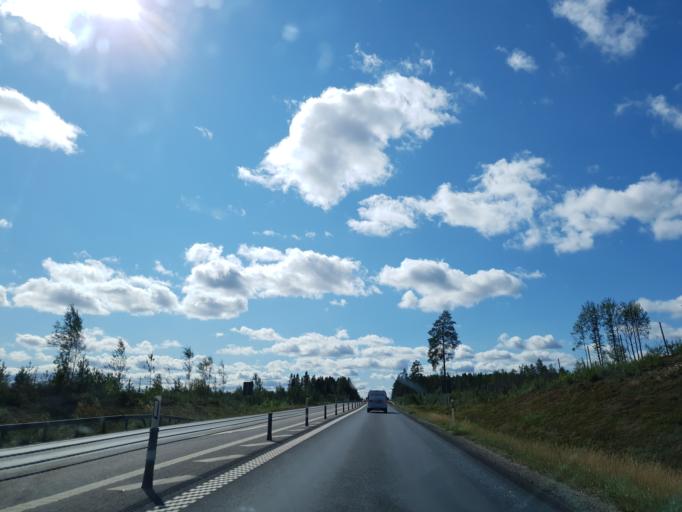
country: SE
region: Vaesterbotten
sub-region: Nordmalings Kommun
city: Nordmaling
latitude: 63.5103
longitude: 19.3551
